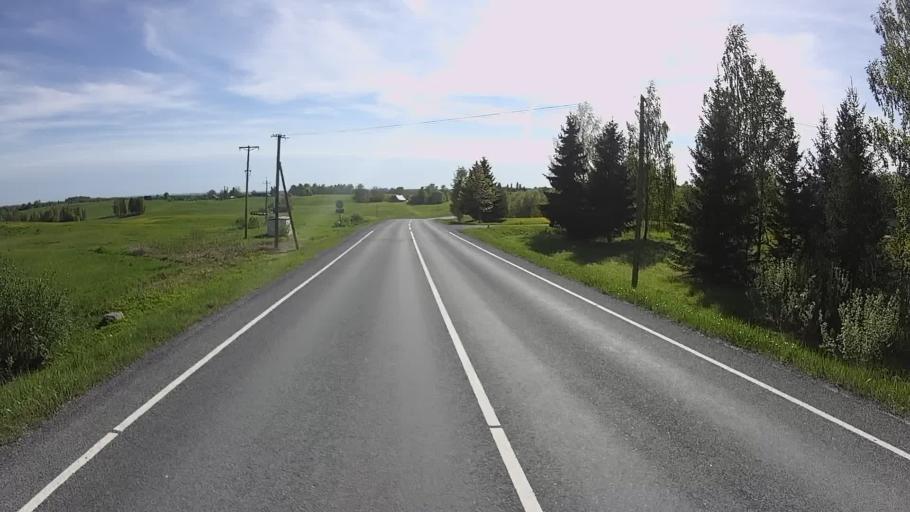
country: EE
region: Vorumaa
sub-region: Antsla vald
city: Vana-Antsla
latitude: 57.9549
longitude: 26.4462
